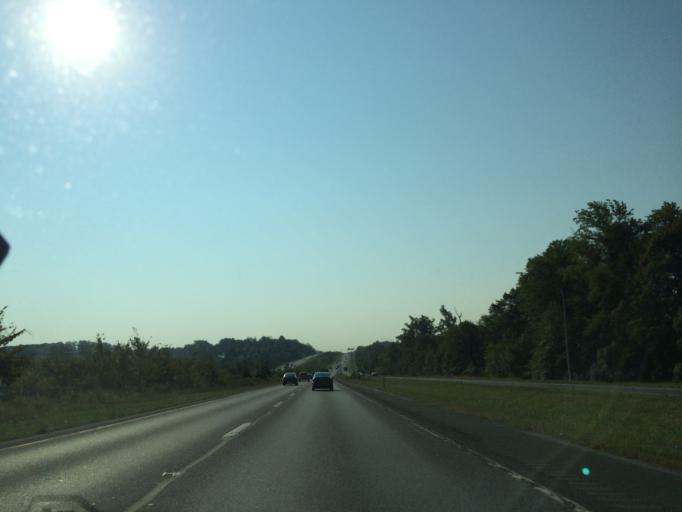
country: US
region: Maryland
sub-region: Howard County
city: Savage
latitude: 39.1374
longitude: -76.8102
